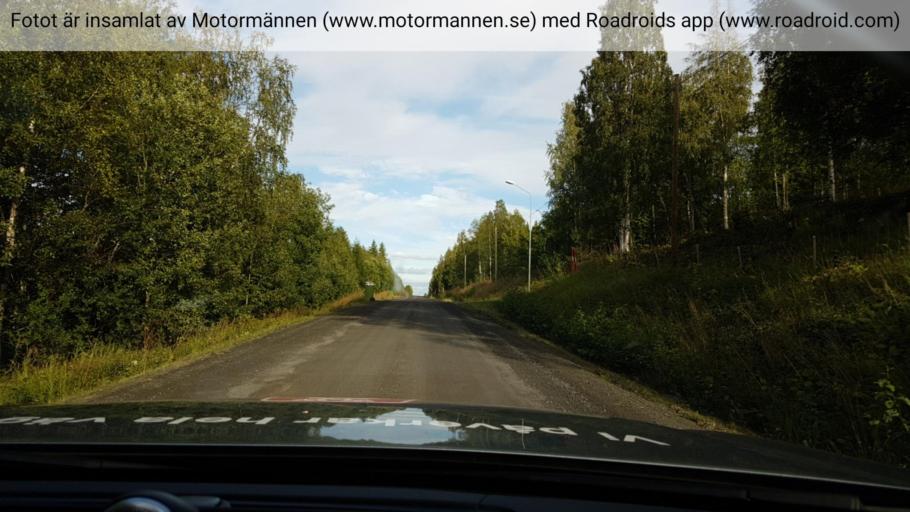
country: SE
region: Jaemtland
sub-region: Stroemsunds Kommun
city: Stroemsund
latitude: 64.1431
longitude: 15.7094
